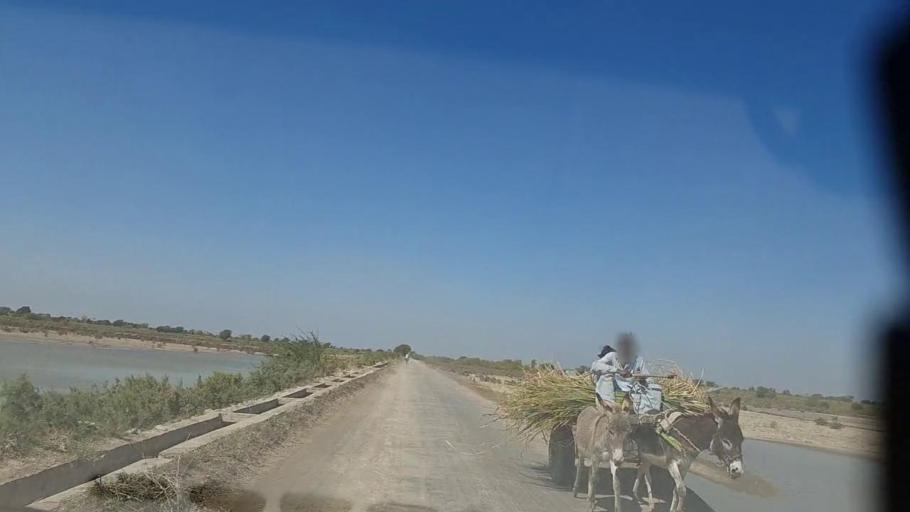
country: PK
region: Sindh
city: Digri
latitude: 25.1692
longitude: 69.0643
